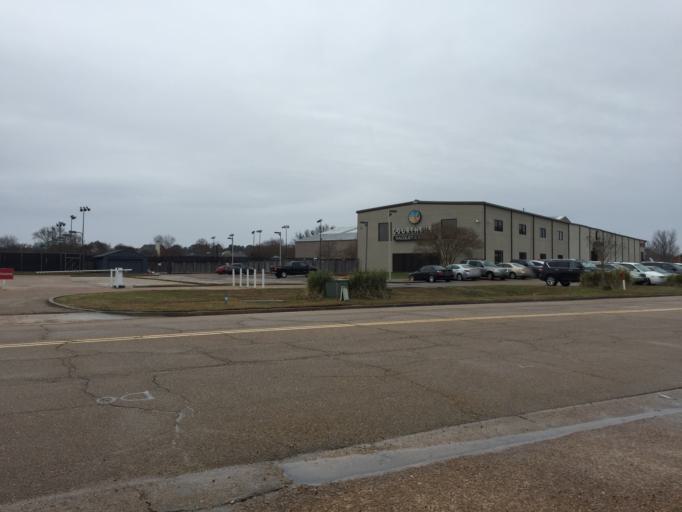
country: US
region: Mississippi
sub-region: Madison County
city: Ridgeland
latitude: 32.3857
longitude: -90.1119
